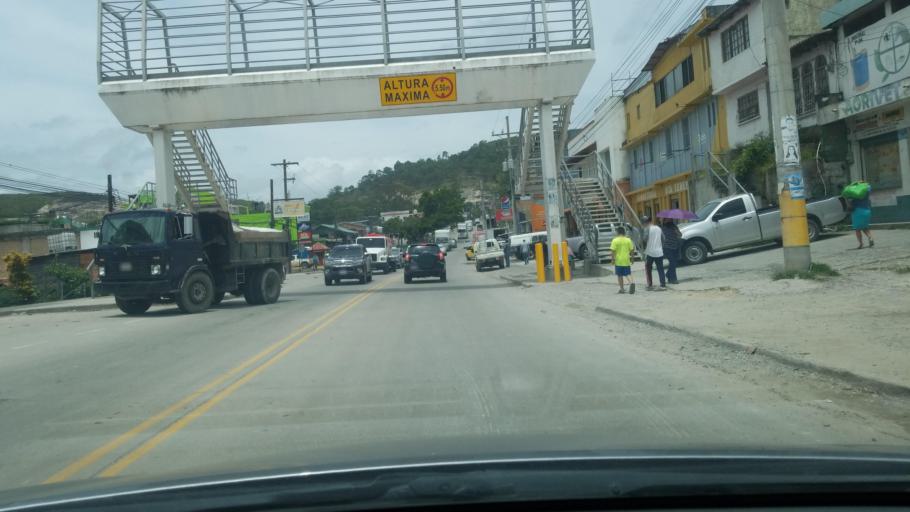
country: HN
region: Copan
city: Santa Rosa de Copan
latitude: 14.7623
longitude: -88.7745
